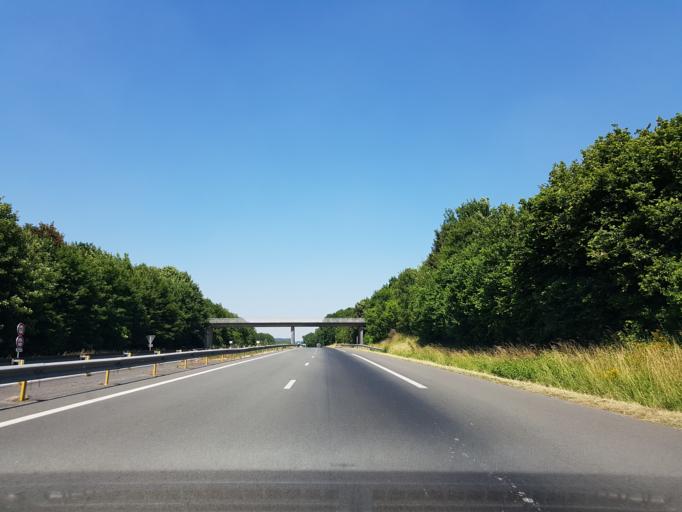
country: FR
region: Nord-Pas-de-Calais
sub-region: Departement du Nord
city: Marcoing
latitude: 50.1353
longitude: 3.1421
